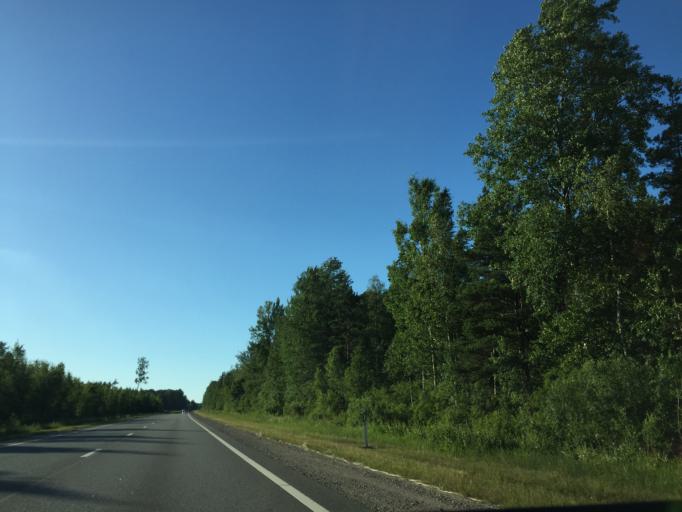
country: LV
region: Ventspils
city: Ventspils
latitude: 57.3817
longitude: 21.7118
